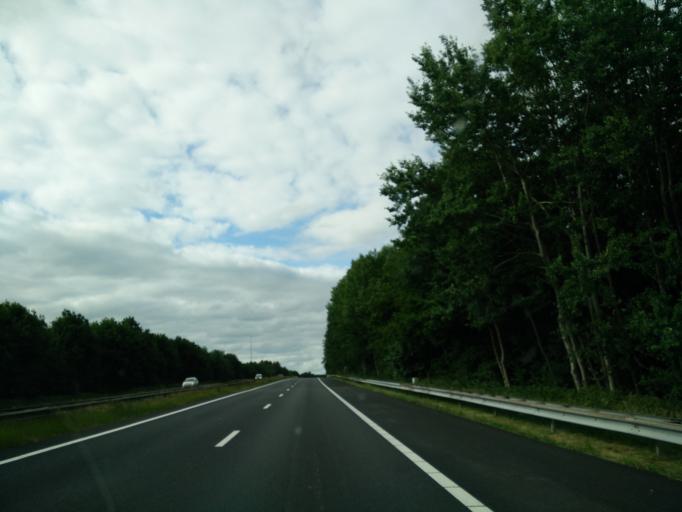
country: NL
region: Drenthe
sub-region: Gemeente Assen
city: Assen
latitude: 52.9913
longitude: 6.5259
